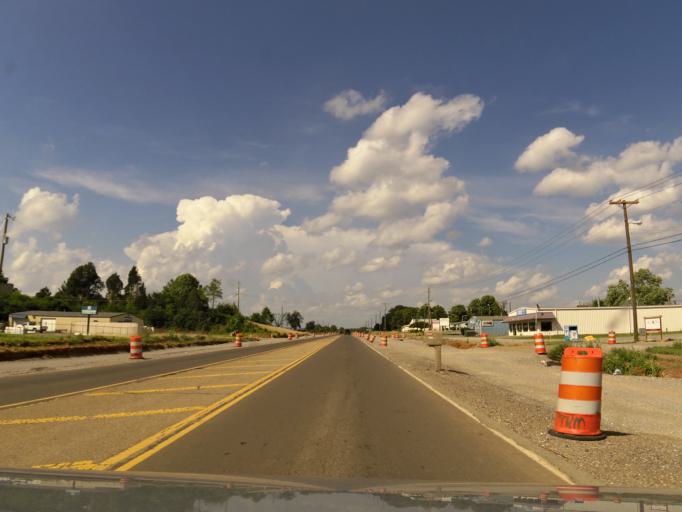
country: US
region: Tennessee
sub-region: Knox County
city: Knoxville
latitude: 36.0941
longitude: -83.9176
